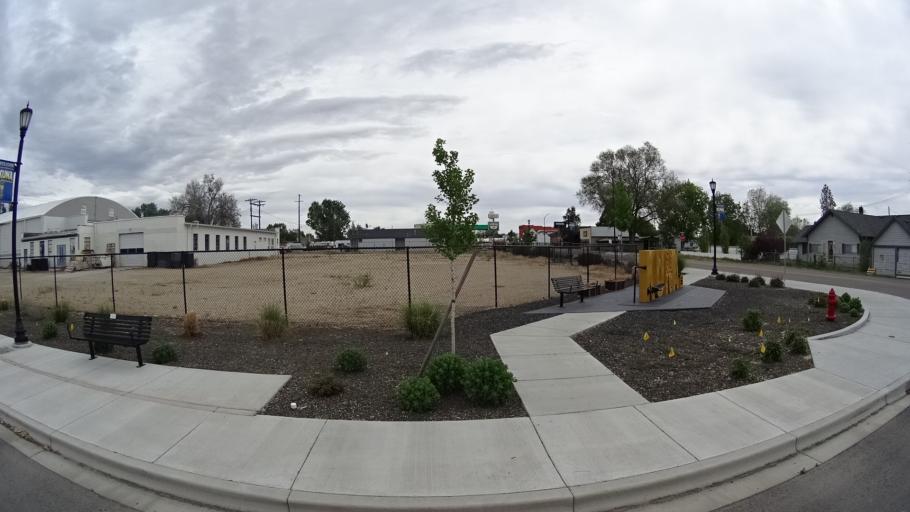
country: US
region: Idaho
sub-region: Ada County
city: Kuna
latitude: 43.4910
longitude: -116.4209
